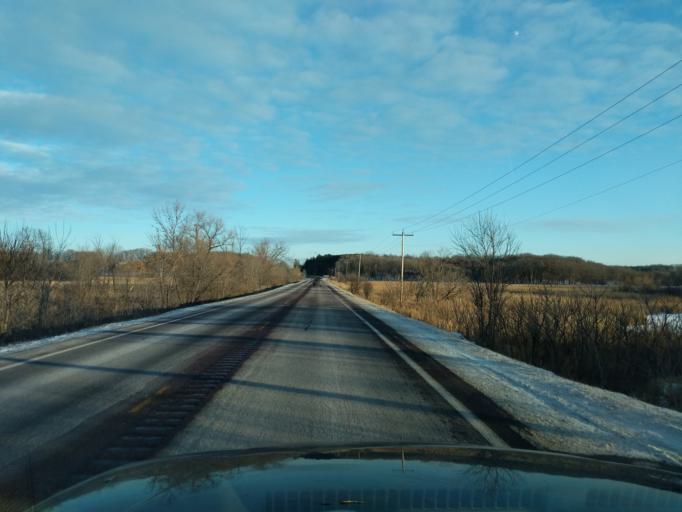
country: US
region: Minnesota
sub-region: Hennepin County
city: Shorewood
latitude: 44.8660
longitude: -93.6162
